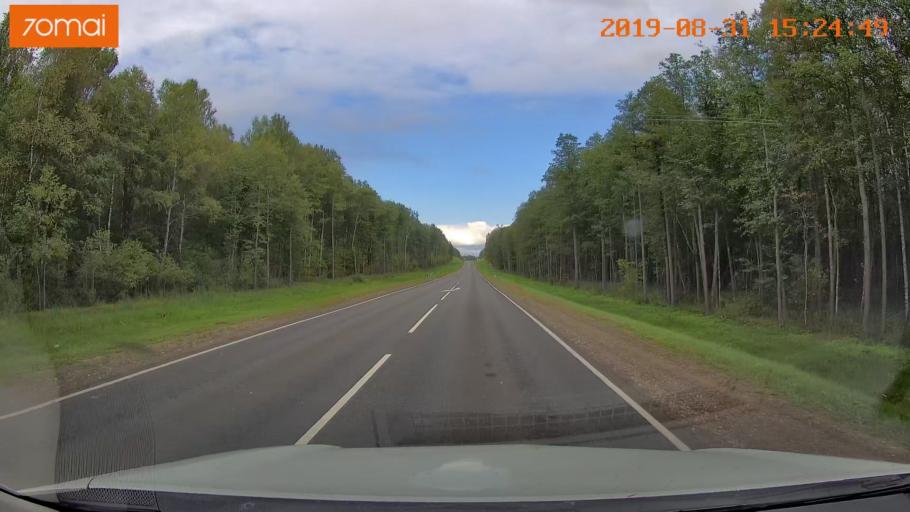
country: RU
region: Kaluga
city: Baryatino
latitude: 54.5329
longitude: 34.5103
